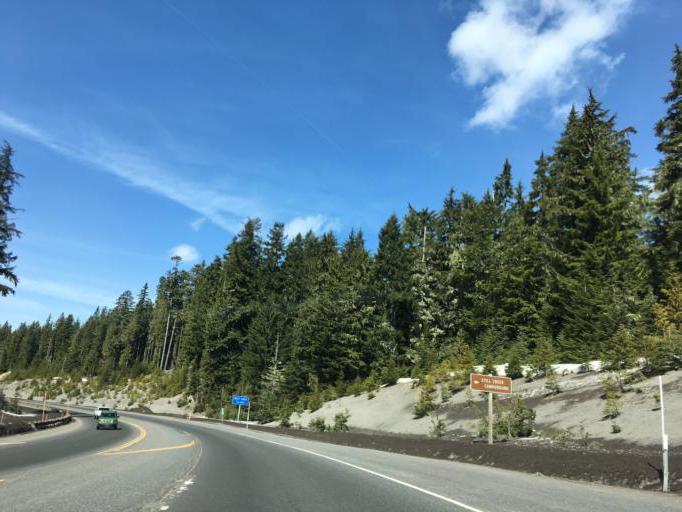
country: US
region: Oregon
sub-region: Clackamas County
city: Mount Hood Village
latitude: 45.3006
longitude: -121.7348
